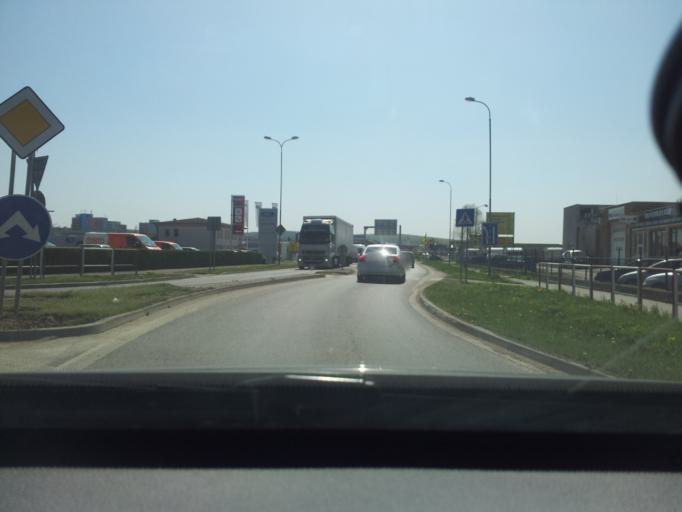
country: SK
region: Nitriansky
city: Banovce nad Bebravou
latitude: 48.7307
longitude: 18.2446
